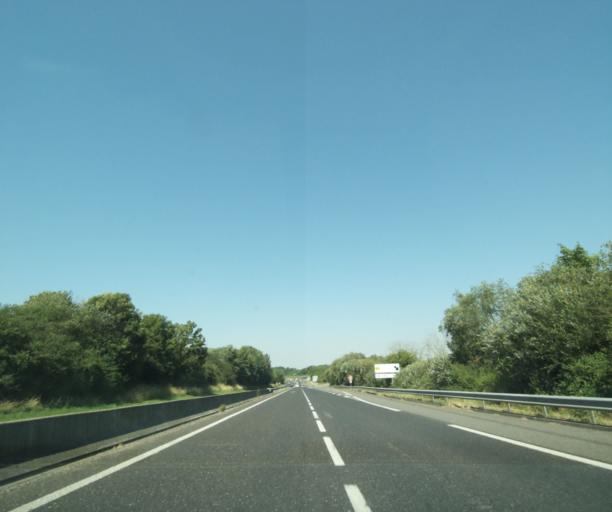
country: FR
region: Lorraine
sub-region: Departement de la Meuse
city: Ancerville
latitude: 48.6395
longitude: 5.0287
